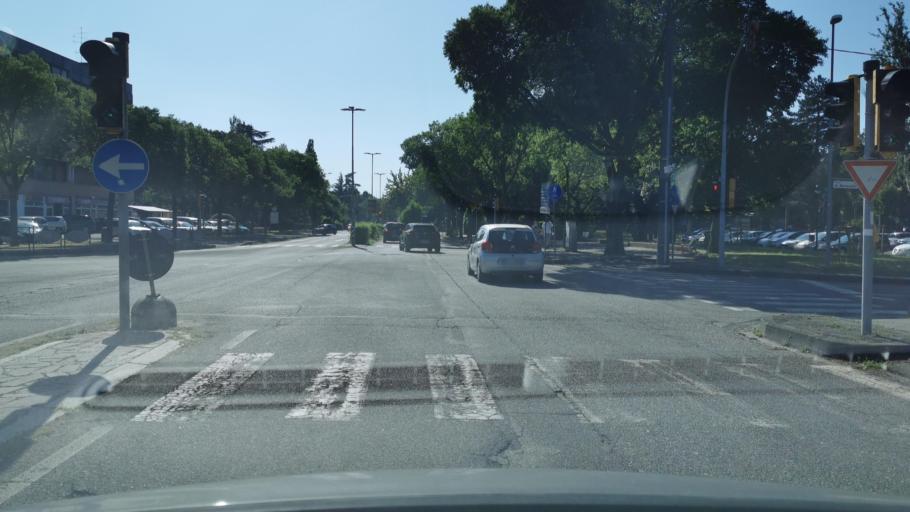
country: IT
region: Emilia-Romagna
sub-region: Provincia di Modena
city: Carpi Centro
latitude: 44.7822
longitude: 10.8781
